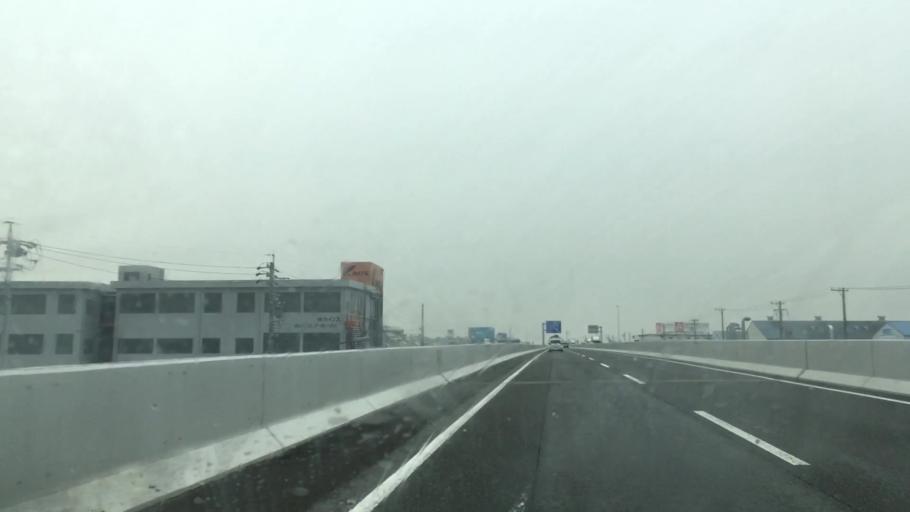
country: JP
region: Aichi
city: Anjo
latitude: 34.9170
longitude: 137.0562
